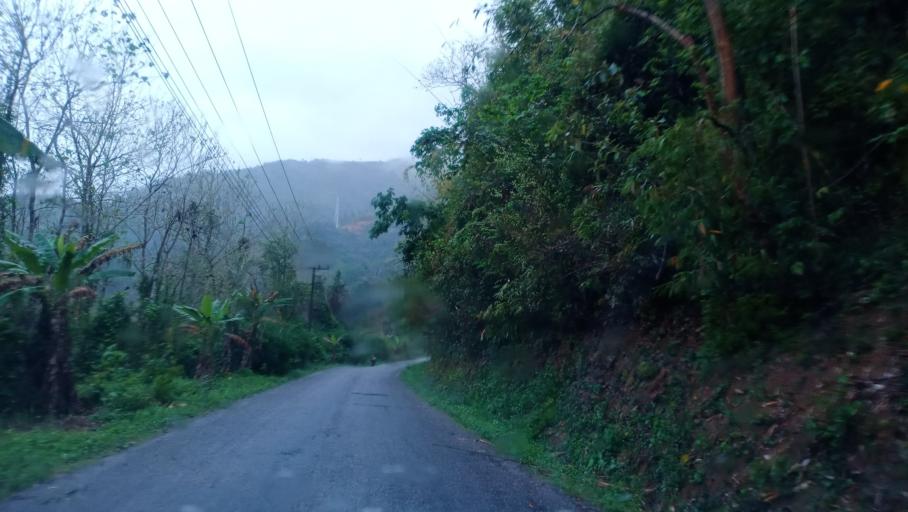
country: LA
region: Phongsali
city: Khoa
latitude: 21.0633
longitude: 102.4806
